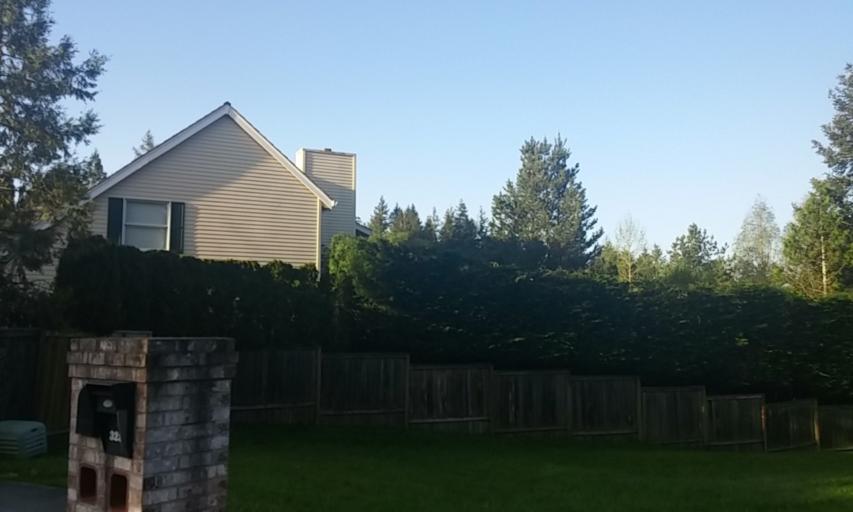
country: US
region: Oregon
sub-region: Washington County
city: Cedar Mill
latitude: 45.5429
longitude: -122.7951
